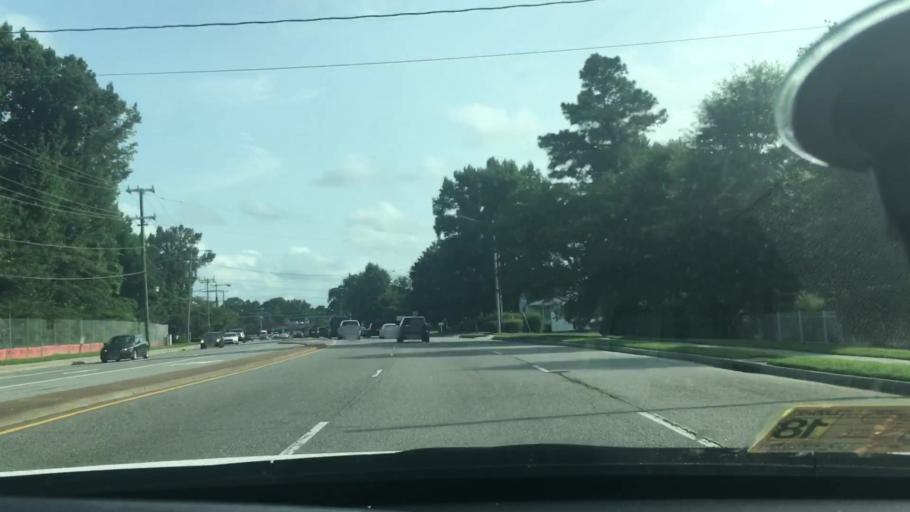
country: US
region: Virginia
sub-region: City of Virginia Beach
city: Virginia Beach
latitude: 36.8443
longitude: -75.9960
